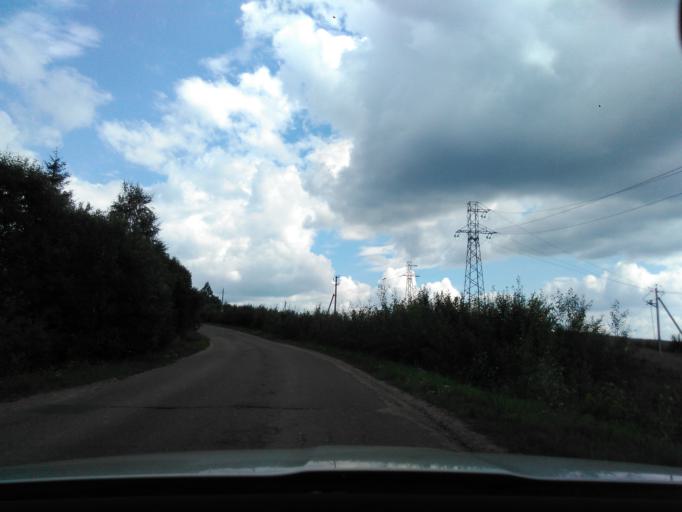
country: RU
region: Moskovskaya
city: Mendeleyevo
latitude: 56.1069
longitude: 37.2445
